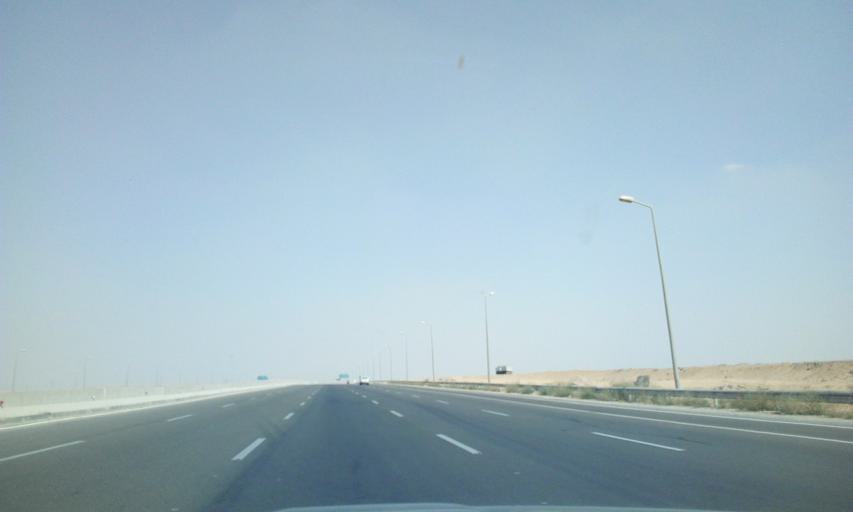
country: EG
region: Muhafazat al Qahirah
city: Halwan
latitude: 29.9055
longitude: 31.7130
